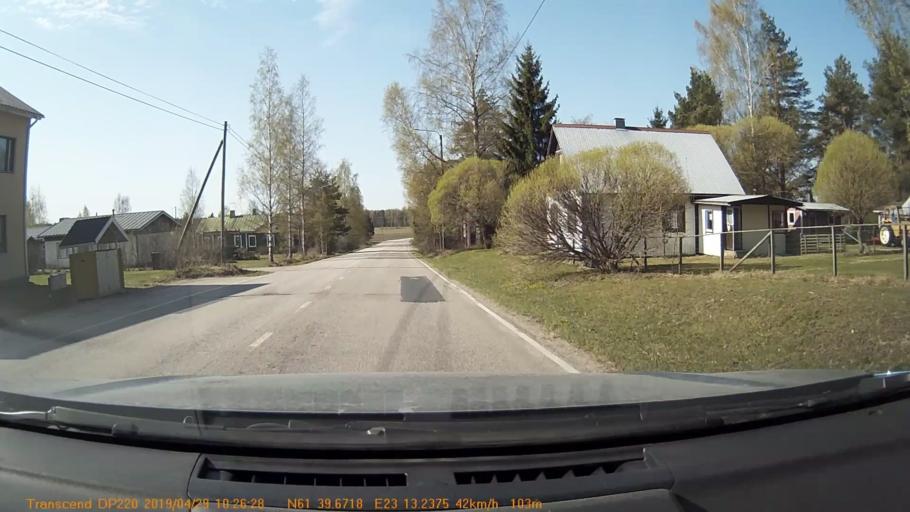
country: FI
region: Pirkanmaa
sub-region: Tampere
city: Haemeenkyroe
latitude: 61.6609
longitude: 23.2202
